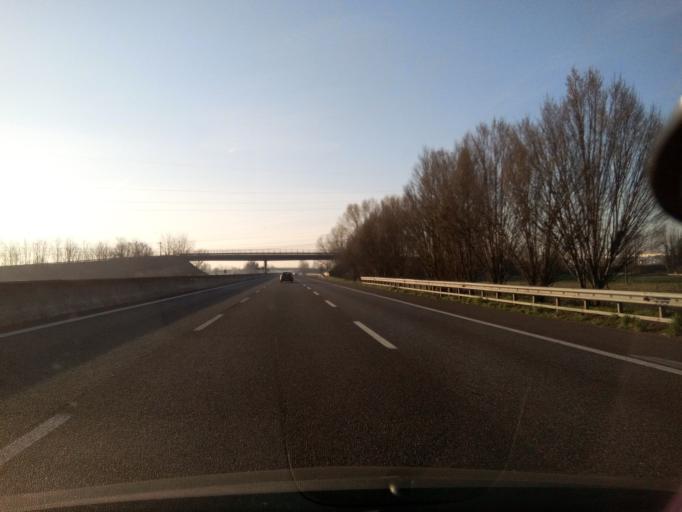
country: IT
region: Lombardy
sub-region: Provincia di Lodi
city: San Rocco al Porto
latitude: 45.0975
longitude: 9.7011
